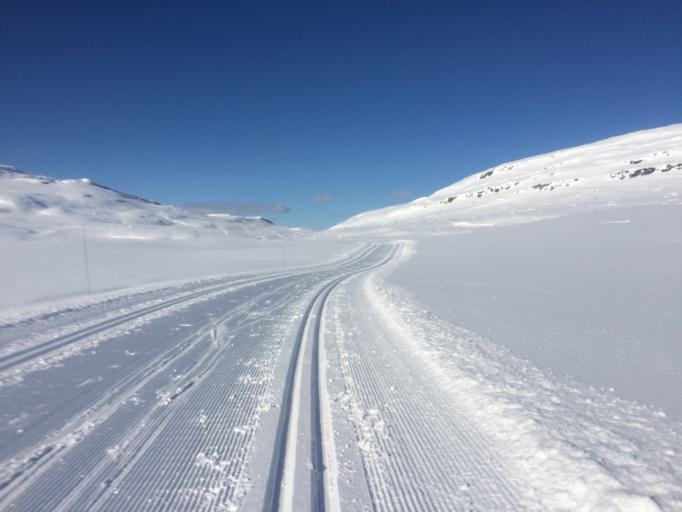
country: NO
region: Oppland
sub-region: Ringebu
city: Ringebu
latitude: 61.3821
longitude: 10.0601
